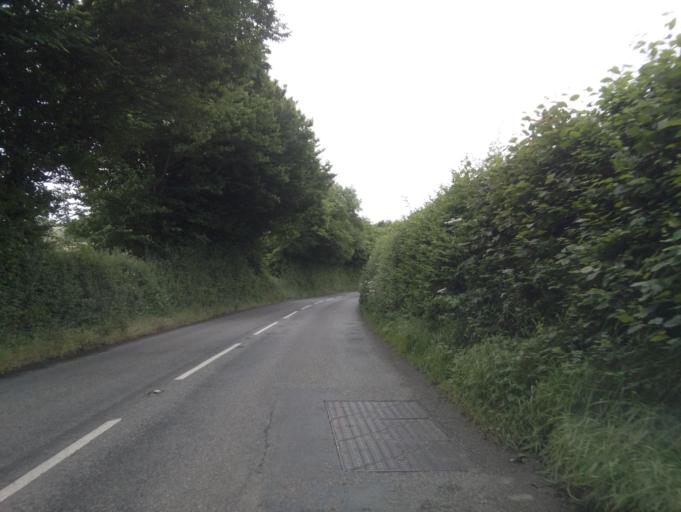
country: GB
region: England
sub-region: Devon
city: Chudleigh
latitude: 50.6698
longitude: -3.6474
